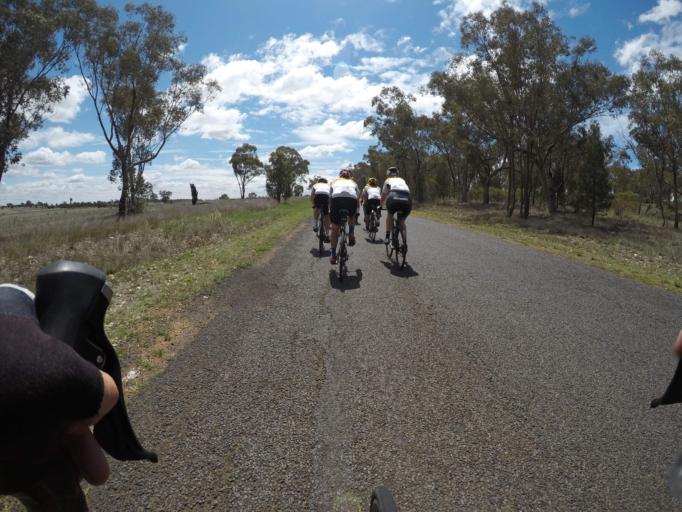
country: AU
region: New South Wales
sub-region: Dubbo Municipality
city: Dubbo
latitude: -32.3748
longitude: 148.5794
